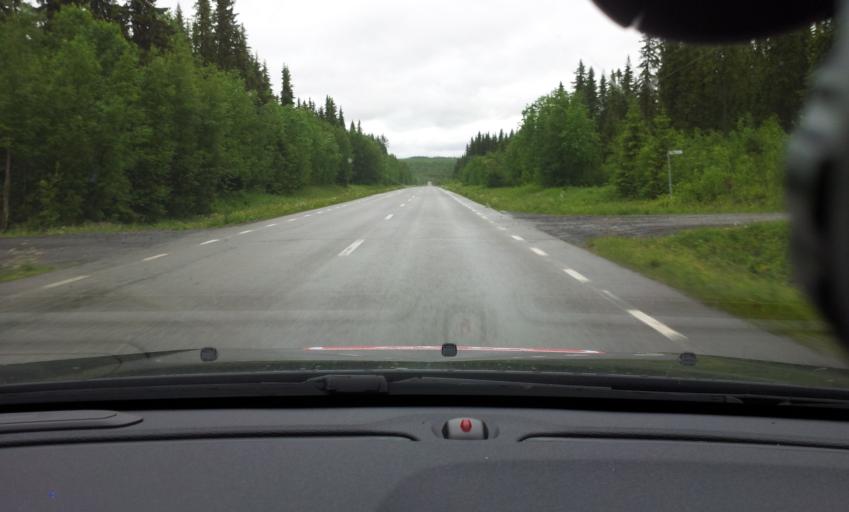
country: SE
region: Jaemtland
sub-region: Krokoms Kommun
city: Krokom
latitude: 63.5355
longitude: 14.5710
